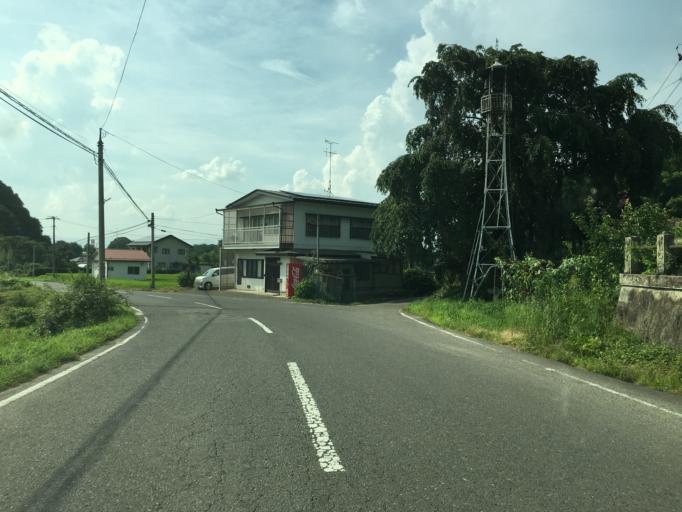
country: JP
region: Fukushima
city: Sukagawa
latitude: 37.3304
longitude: 140.4171
